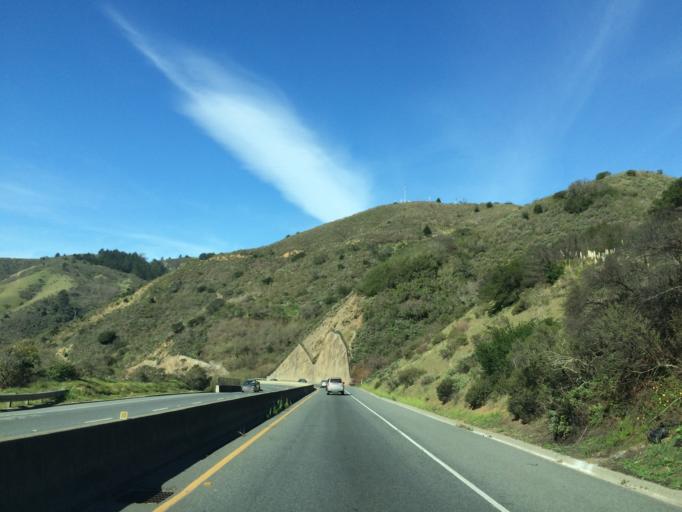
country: US
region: California
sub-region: San Mateo County
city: Highlands-Baywood Park
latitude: 37.4922
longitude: -122.3770
